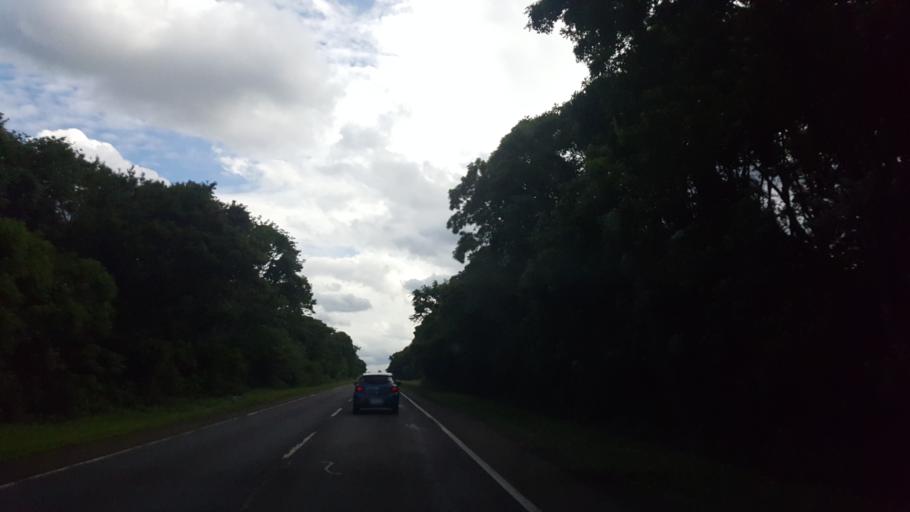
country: AR
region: Misiones
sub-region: Departamento de Iguazu
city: Puerto Iguazu
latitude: -25.7085
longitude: -54.5168
